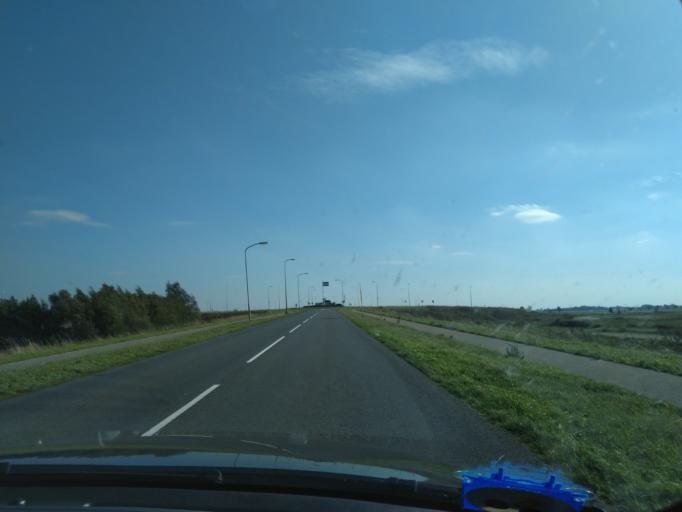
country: NL
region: Groningen
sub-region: Gemeente Veendam
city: Veendam
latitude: 53.0792
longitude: 6.8796
